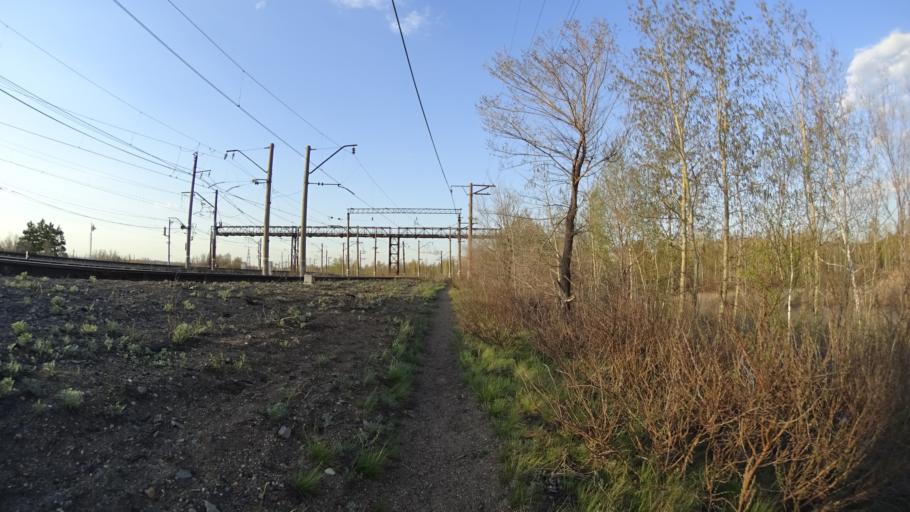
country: RU
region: Chelyabinsk
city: Troitsk
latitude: 54.0566
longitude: 61.6130
